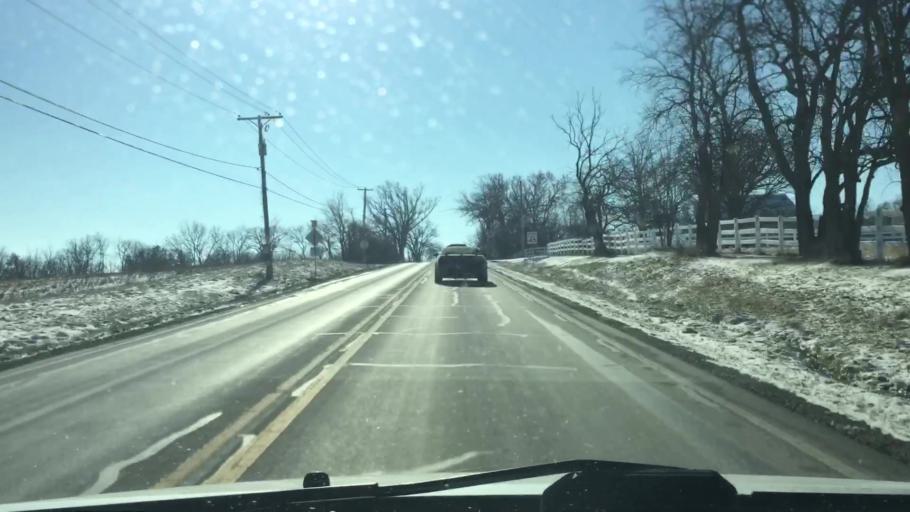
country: US
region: Illinois
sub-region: DuPage County
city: Wayne
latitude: 41.9668
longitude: -88.2633
